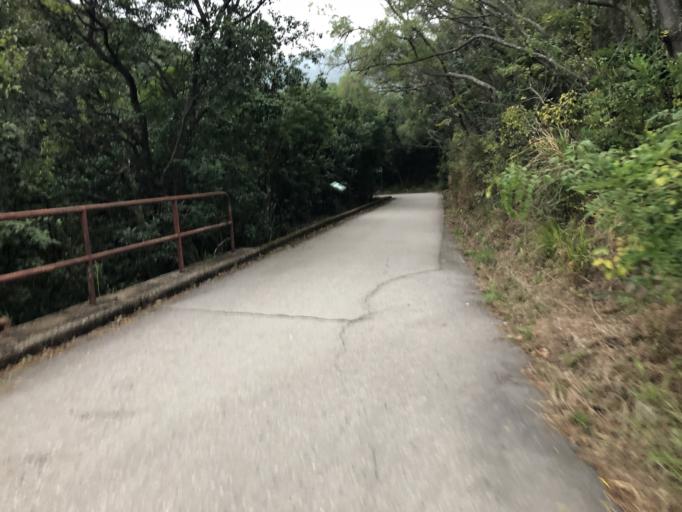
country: HK
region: Wanchai
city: Wan Chai
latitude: 22.2600
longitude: 114.2139
